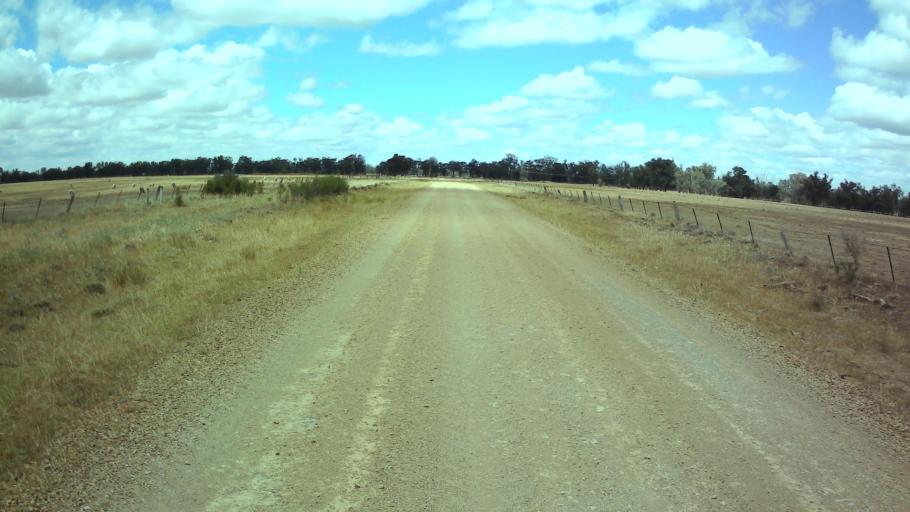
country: AU
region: New South Wales
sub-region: Weddin
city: Grenfell
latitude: -34.0260
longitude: 147.9135
